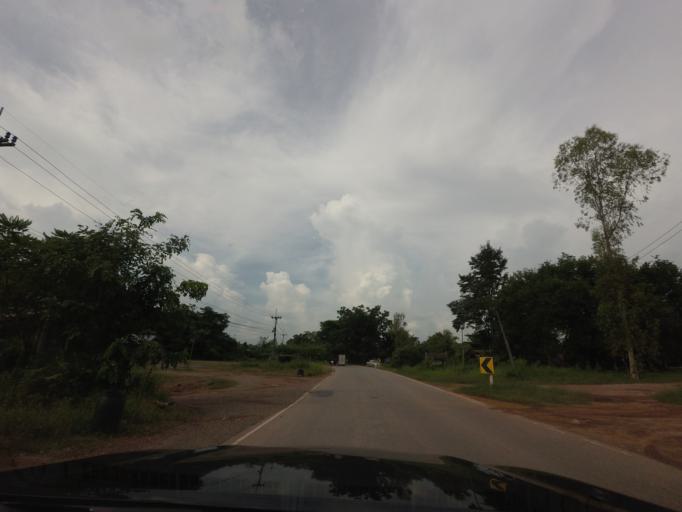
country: TH
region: Changwat Nong Bua Lamphu
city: Suwannakhuha
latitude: 17.4508
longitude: 102.3464
